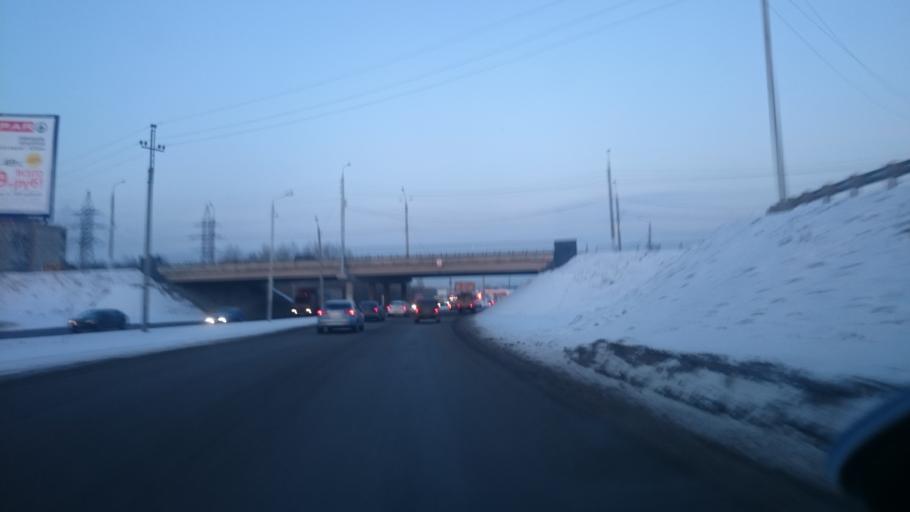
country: RU
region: Tula
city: Tula
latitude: 54.1709
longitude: 37.6362
